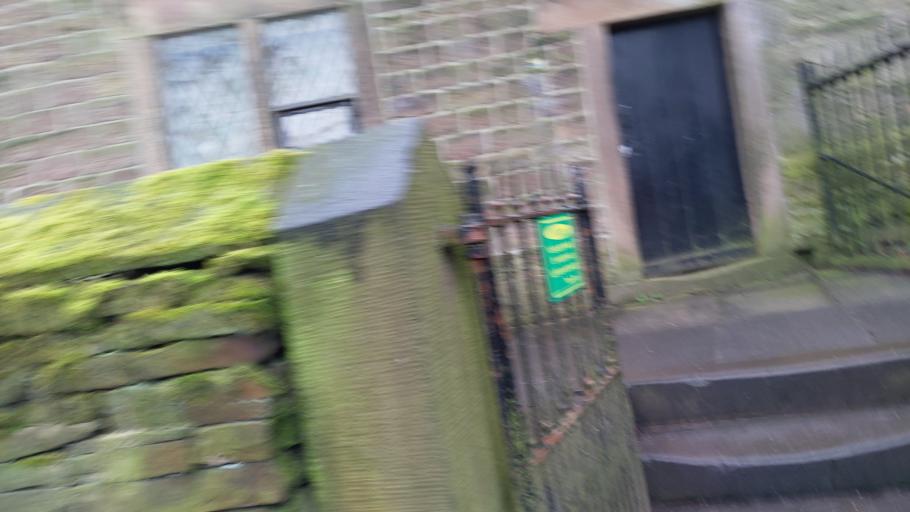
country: GB
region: England
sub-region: Borough of Bolton
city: Horwich
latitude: 53.6261
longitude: -2.5656
